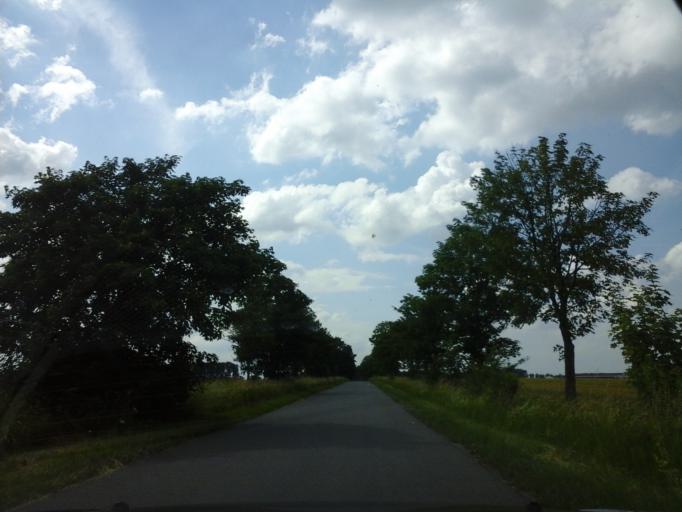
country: PL
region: West Pomeranian Voivodeship
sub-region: Powiat choszczenski
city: Pelczyce
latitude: 53.0797
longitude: 15.3697
